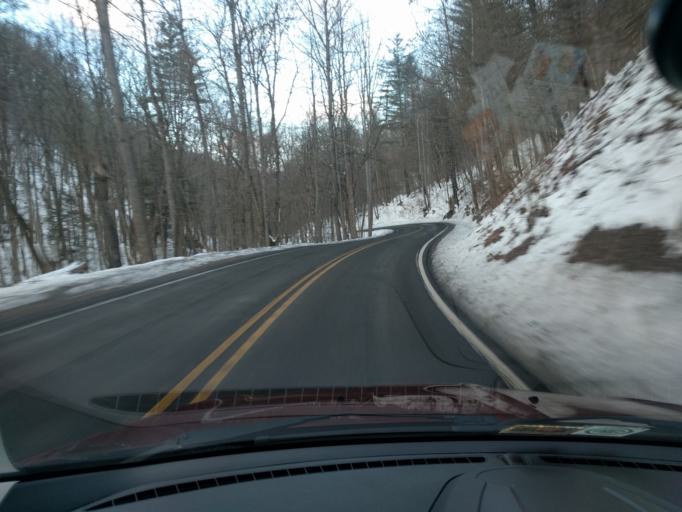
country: US
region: Virginia
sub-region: Bath County
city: Warm Springs
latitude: 38.0836
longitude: -79.8626
